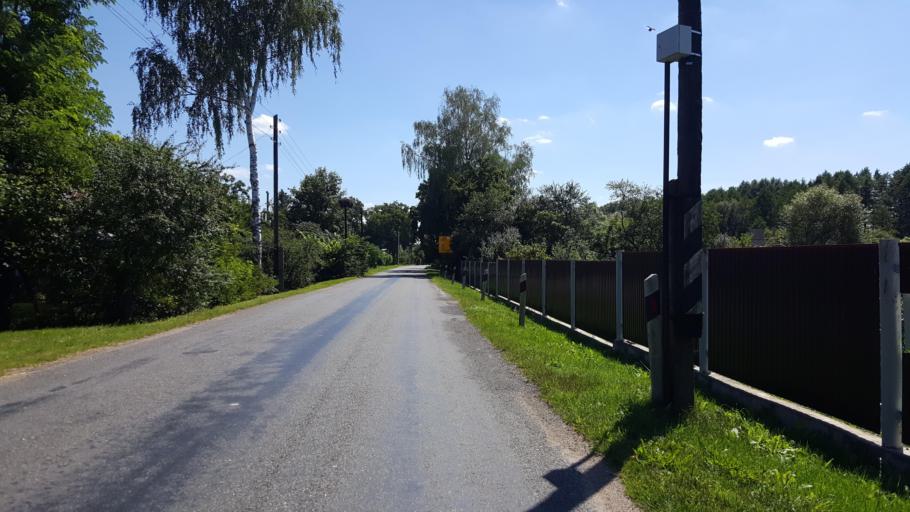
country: BY
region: Brest
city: Charnawchytsy
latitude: 52.3264
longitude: 23.6103
